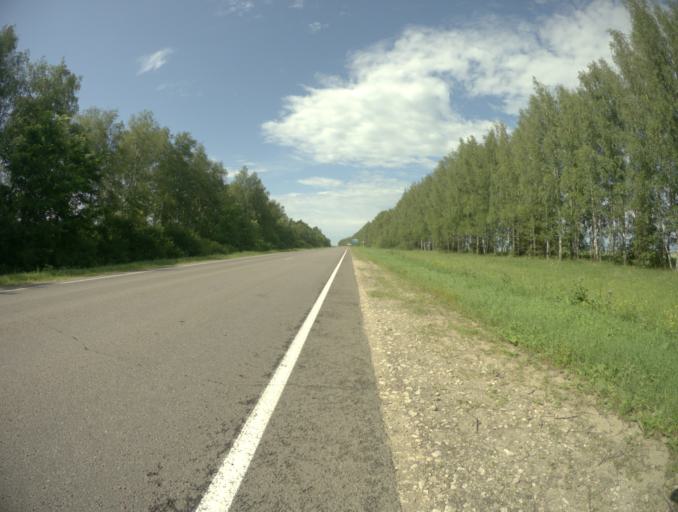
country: RU
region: Vladimir
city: Suzdal'
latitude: 56.3932
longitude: 40.4512
